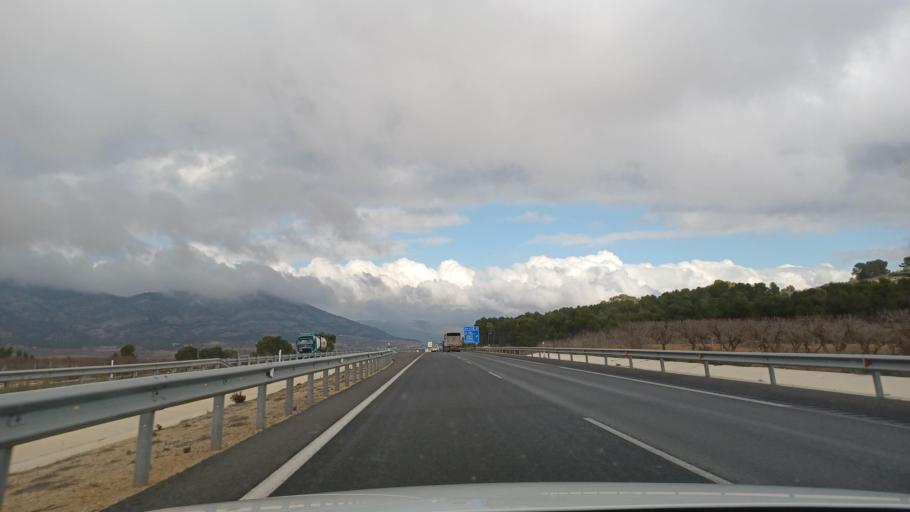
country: ES
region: Valencia
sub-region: Provincia de Valencia
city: La Font de la Figuera
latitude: 38.7703
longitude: -0.8937
